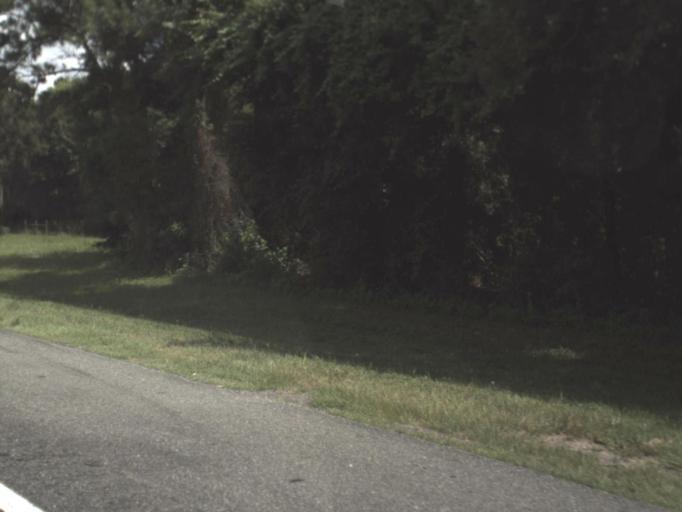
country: US
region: Florida
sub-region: Suwannee County
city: Wellborn
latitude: 30.2516
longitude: -82.7457
